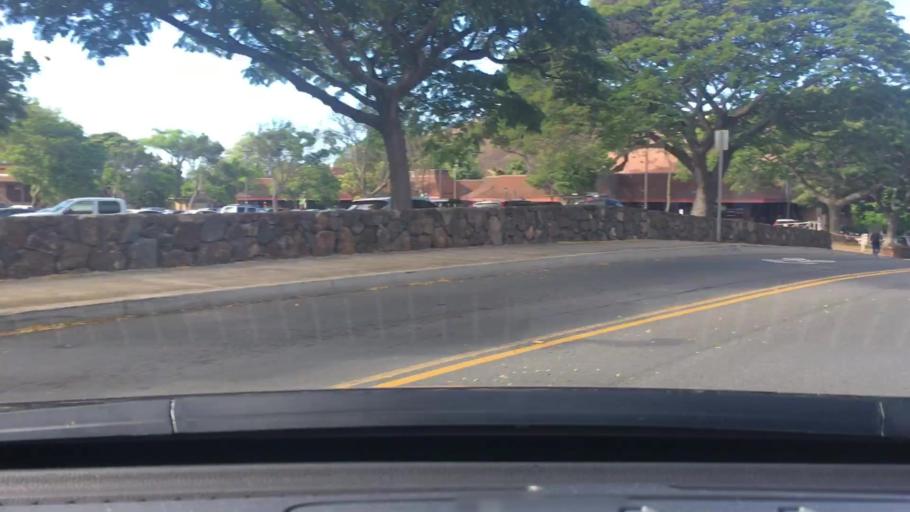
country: US
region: Hawaii
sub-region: Honolulu County
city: Honolulu
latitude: 21.2733
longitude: -157.8008
